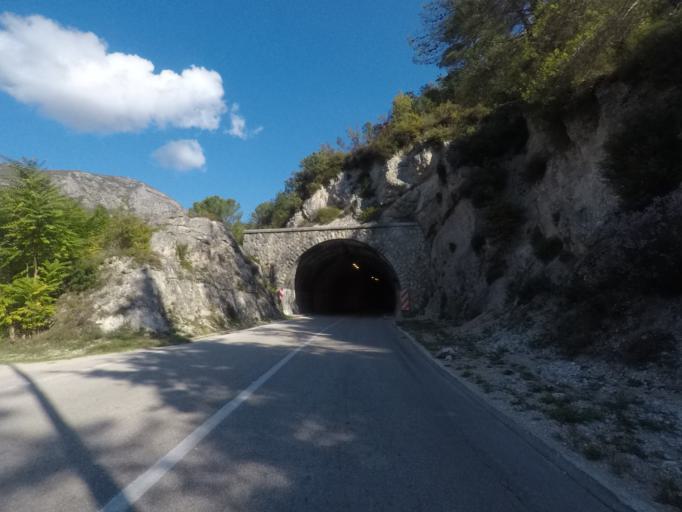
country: BA
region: Republika Srpska
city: Trebinje
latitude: 42.7075
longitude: 18.4818
